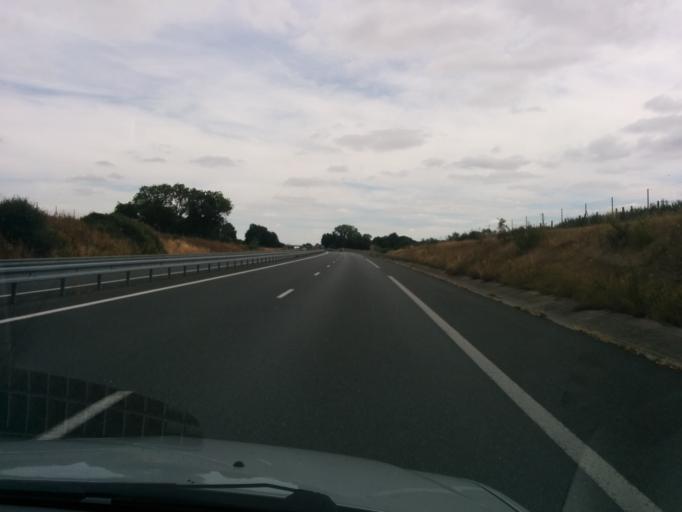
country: FR
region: Poitou-Charentes
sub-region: Departement des Deux-Sevres
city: Saint-Pierre-des-Echaubrognes
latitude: 46.9530
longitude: -0.7737
